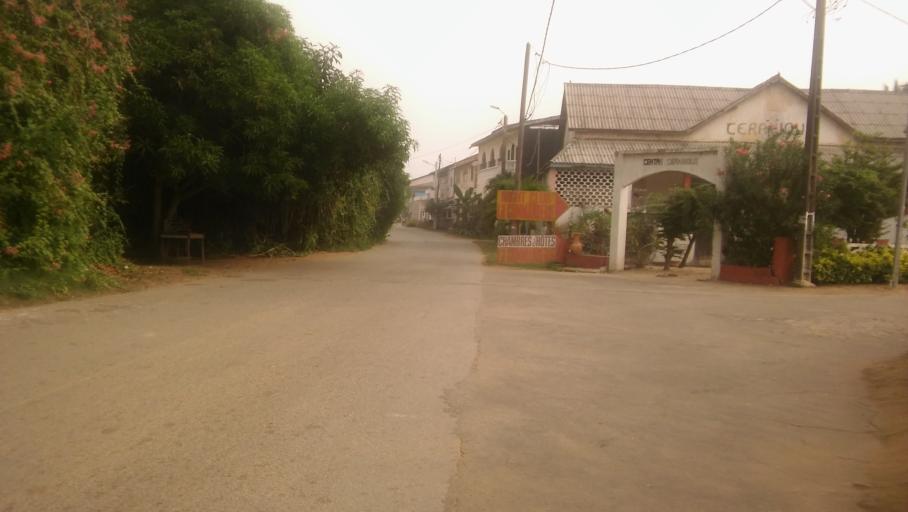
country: CI
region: Sud-Comoe
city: Grand-Bassam
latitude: 5.1950
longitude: -3.7324
